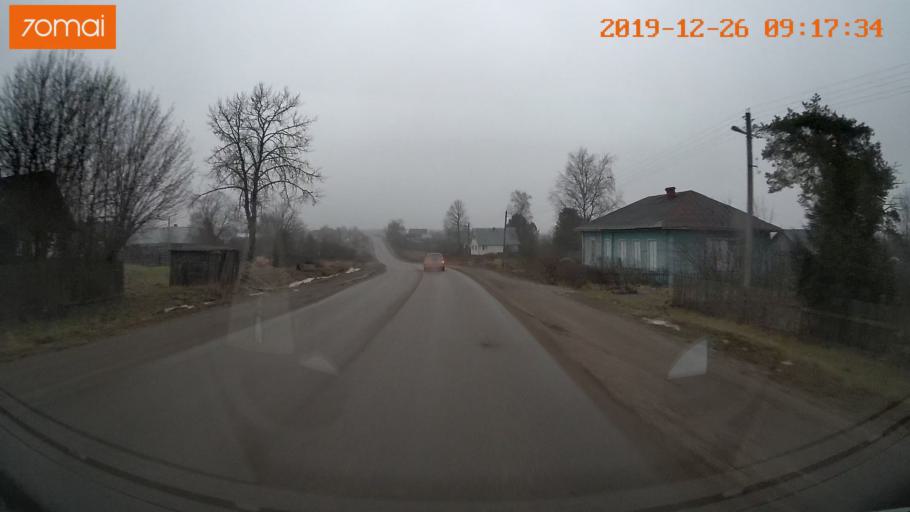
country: RU
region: Vologda
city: Gryazovets
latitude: 58.9309
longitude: 40.2402
